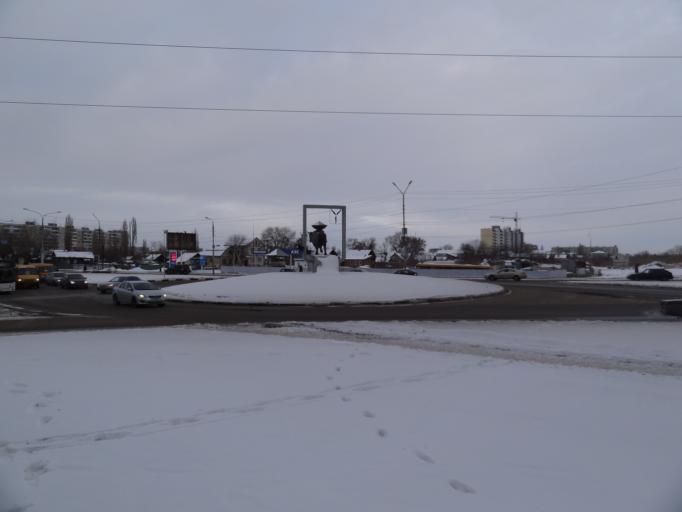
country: RU
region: Saratov
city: Engel's
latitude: 51.4853
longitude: 46.1268
